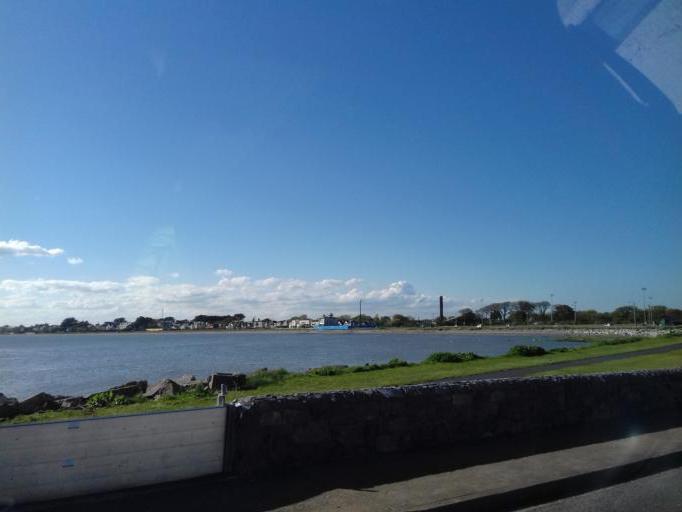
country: IE
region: Leinster
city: Sutton
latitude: 53.3834
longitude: -6.1012
